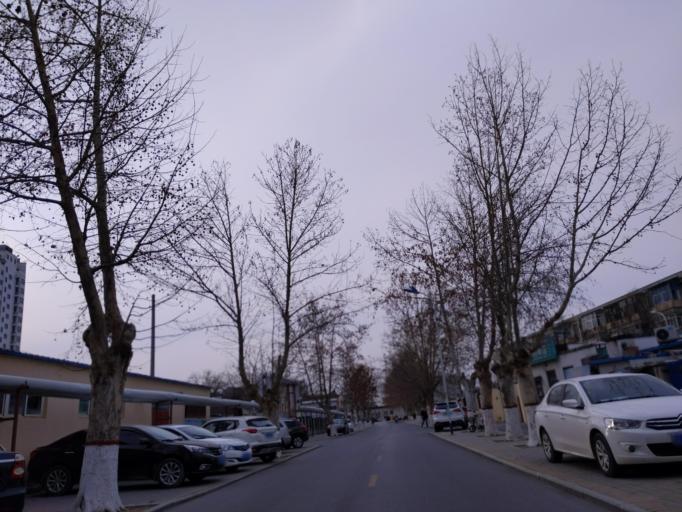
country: CN
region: Henan Sheng
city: Zhongyuanlu
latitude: 35.7599
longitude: 115.0435
